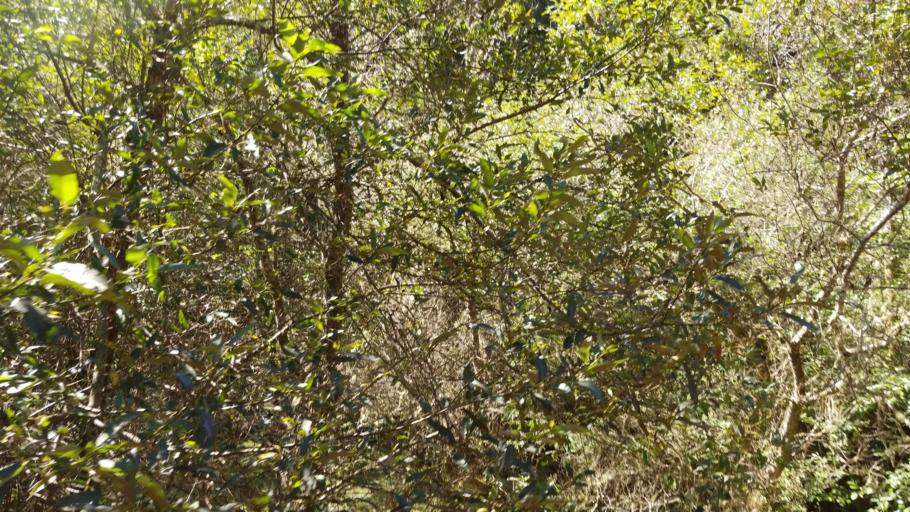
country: US
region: California
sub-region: Mendocino County
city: Fort Bragg
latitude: 39.4487
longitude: -123.7817
